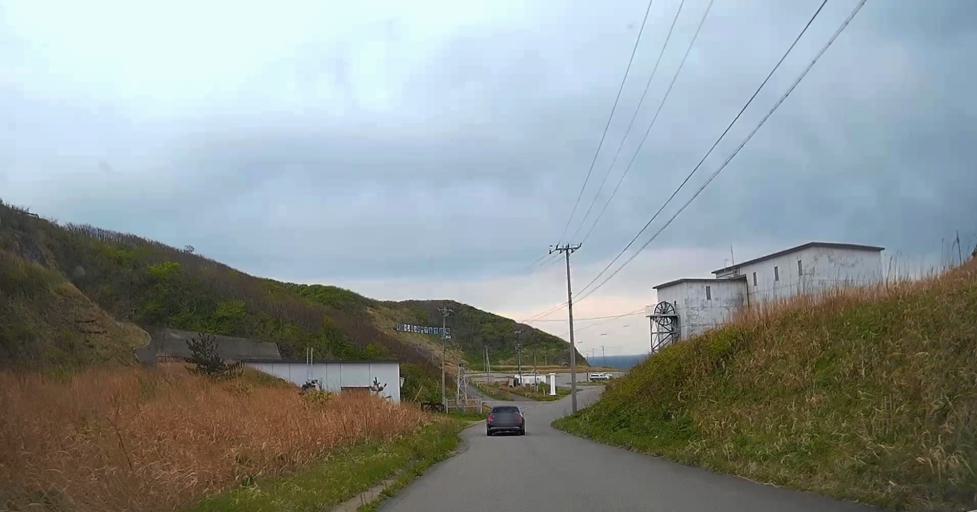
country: JP
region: Aomori
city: Shimokizukuri
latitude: 41.2540
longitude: 140.3480
